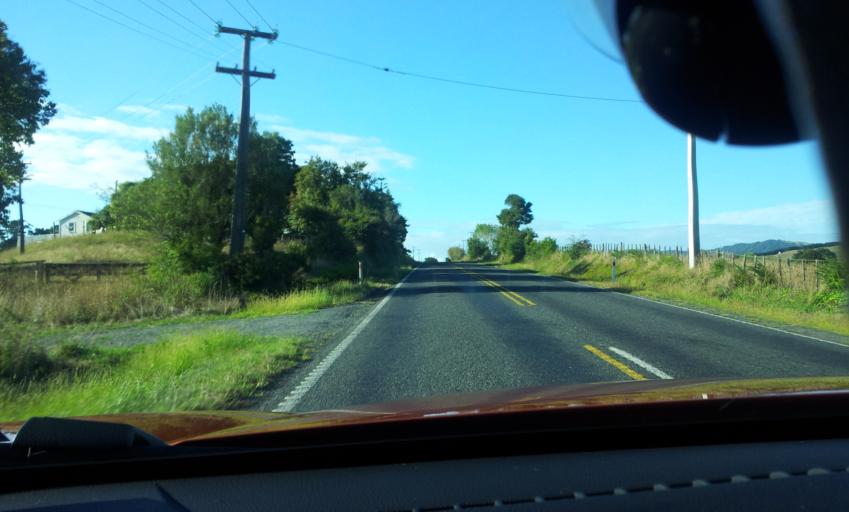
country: NZ
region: Waikato
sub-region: Hauraki District
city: Ngatea
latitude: -37.3038
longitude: 175.3783
